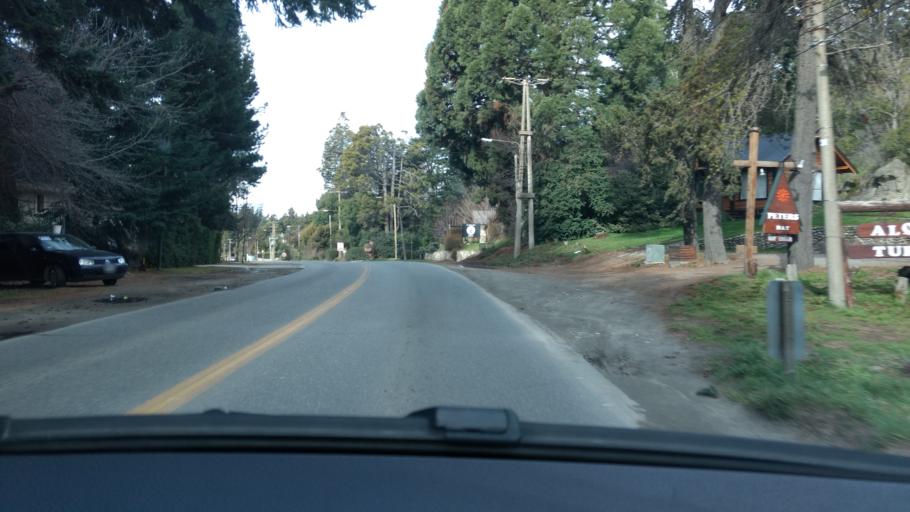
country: AR
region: Rio Negro
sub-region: Departamento de Bariloche
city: San Carlos de Bariloche
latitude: -41.1213
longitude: -71.3758
